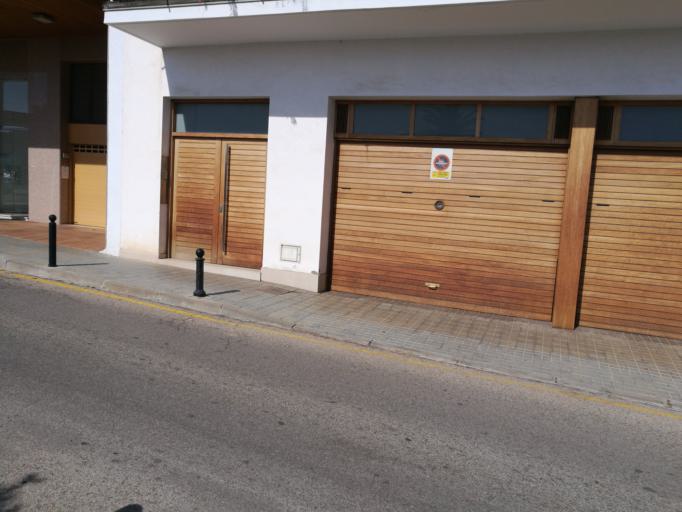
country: ES
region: Catalonia
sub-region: Provincia de Girona
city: Blanes
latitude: 41.6761
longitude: 2.7991
